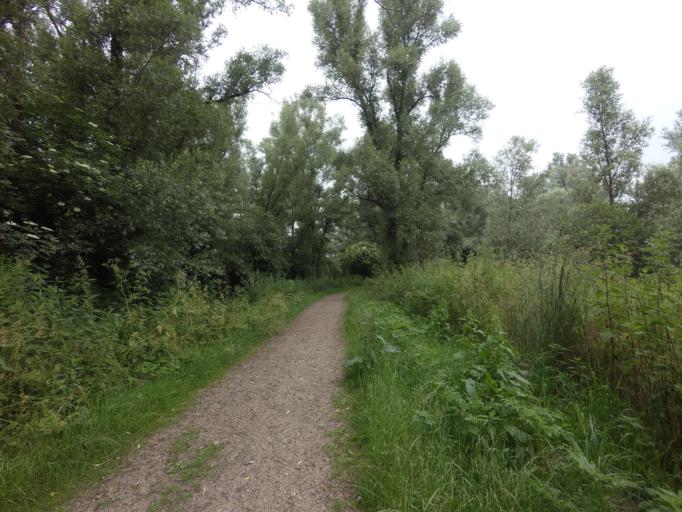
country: NL
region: Flevoland
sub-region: Gemeente Almere
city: Almere Stad
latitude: 52.4126
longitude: 5.3322
